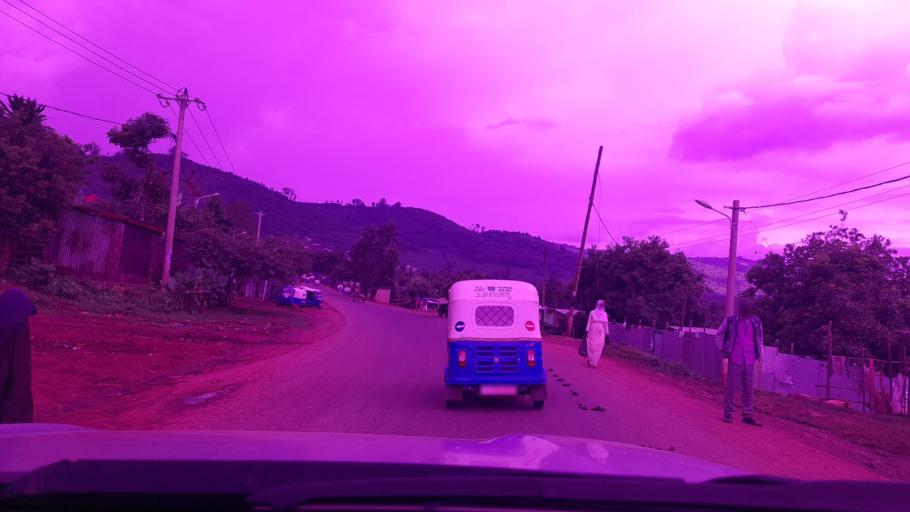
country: ET
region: Oromiya
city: Jima
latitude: 7.6693
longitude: 36.8611
